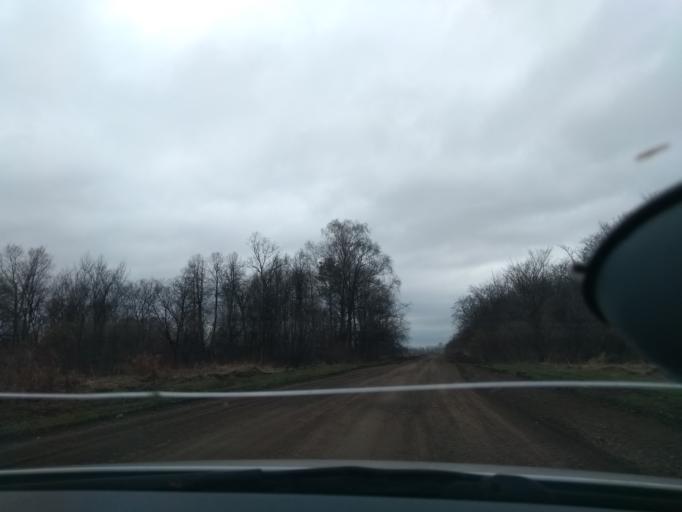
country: RU
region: Perm
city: Orda
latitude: 57.2416
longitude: 56.6108
